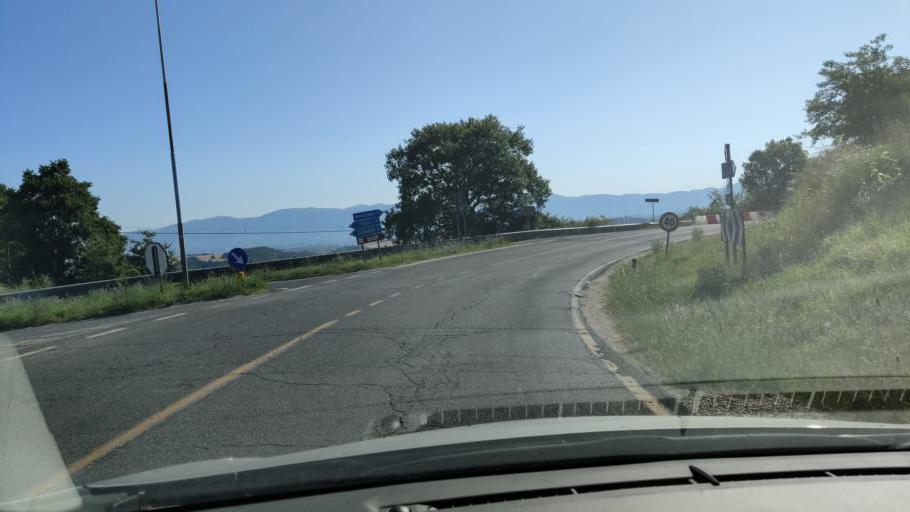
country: IT
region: Umbria
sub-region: Provincia di Terni
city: Avigliano Umbro
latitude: 42.6714
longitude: 12.4448
